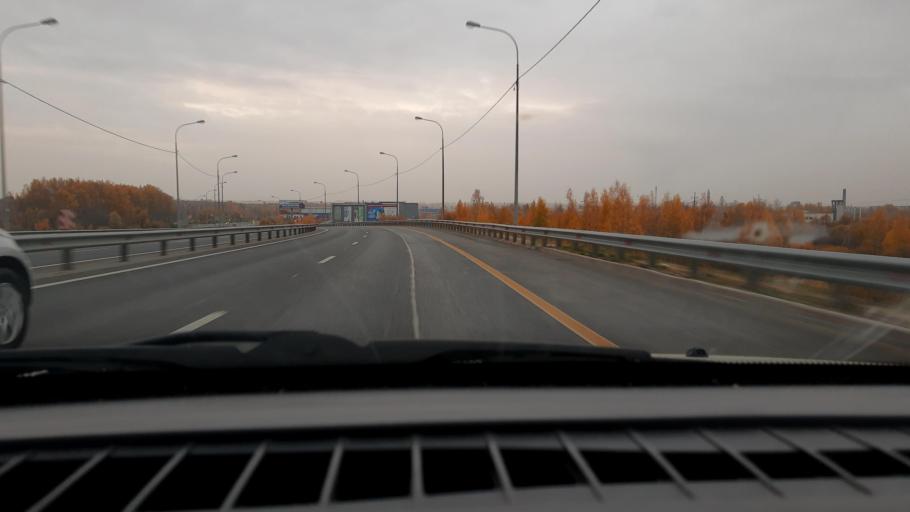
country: RU
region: Nizjnij Novgorod
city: Burevestnik
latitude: 56.1772
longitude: 43.9132
